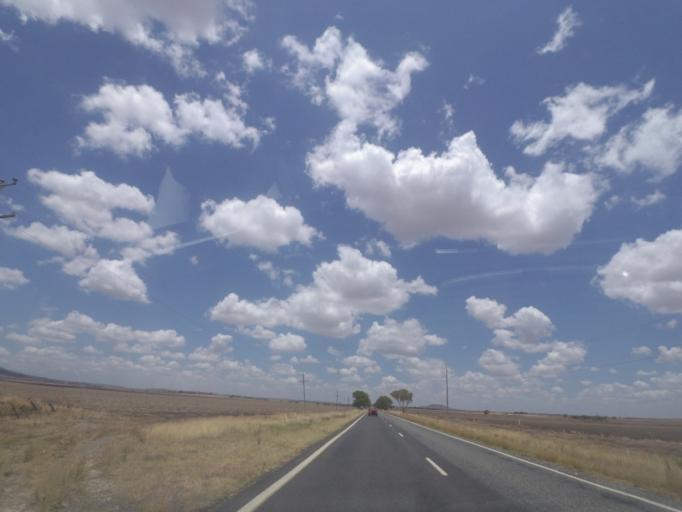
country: AU
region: Queensland
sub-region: Toowoomba
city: Top Camp
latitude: -27.9139
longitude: 151.9806
